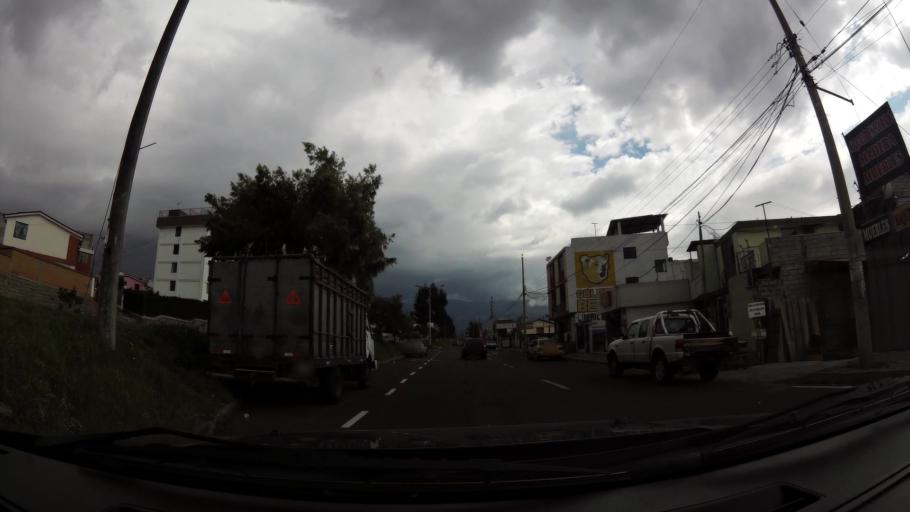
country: EC
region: Pichincha
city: Quito
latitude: -0.0835
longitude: -78.4705
